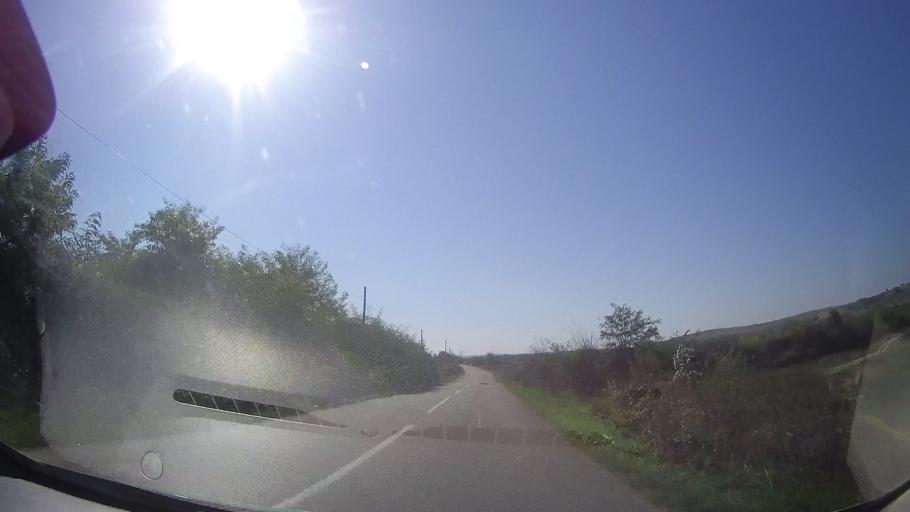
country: RO
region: Timis
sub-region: Comuna Bethausen
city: Bethausen
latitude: 45.8532
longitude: 21.9657
